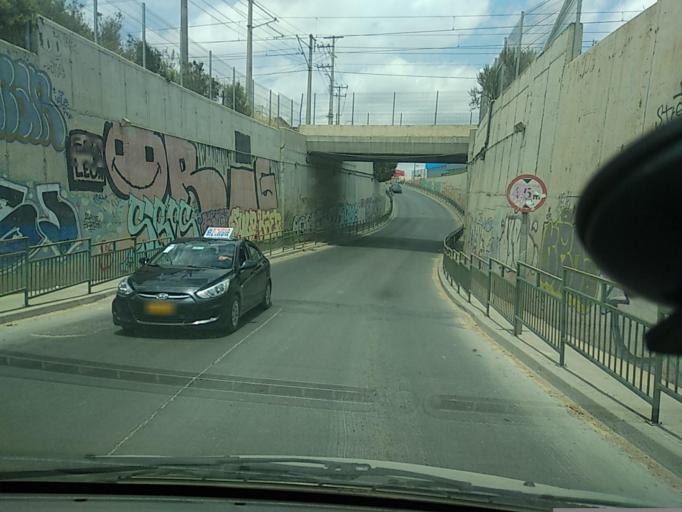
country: CL
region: Valparaiso
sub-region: Provincia de Marga Marga
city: Quilpue
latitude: -33.0409
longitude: -71.4196
